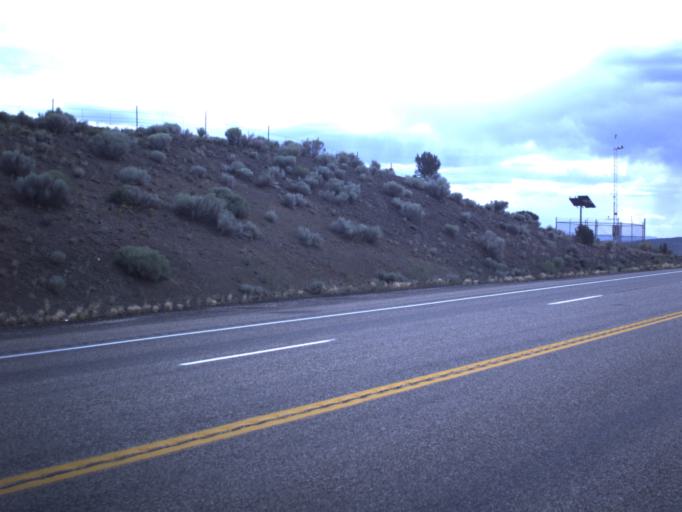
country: US
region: Utah
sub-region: Garfield County
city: Panguitch
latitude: 38.0311
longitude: -112.5310
